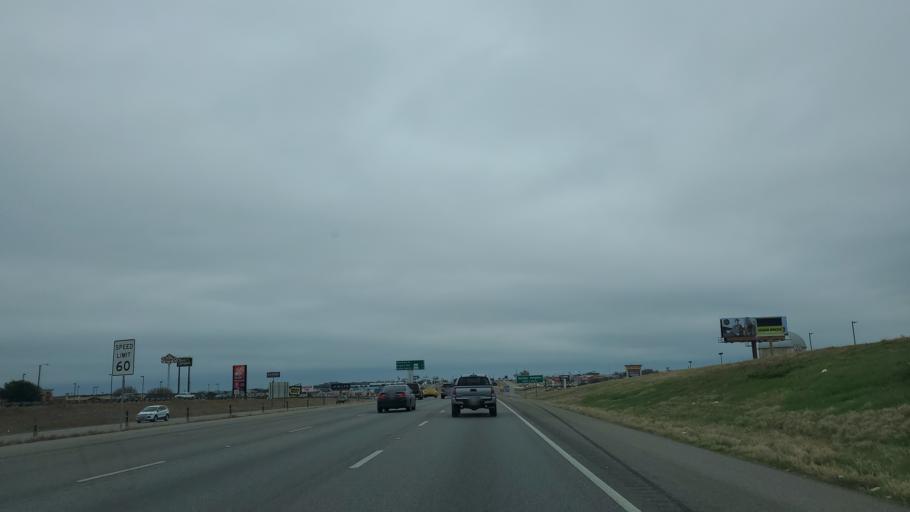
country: US
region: Texas
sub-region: Bell County
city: Killeen
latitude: 31.0870
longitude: -97.7123
